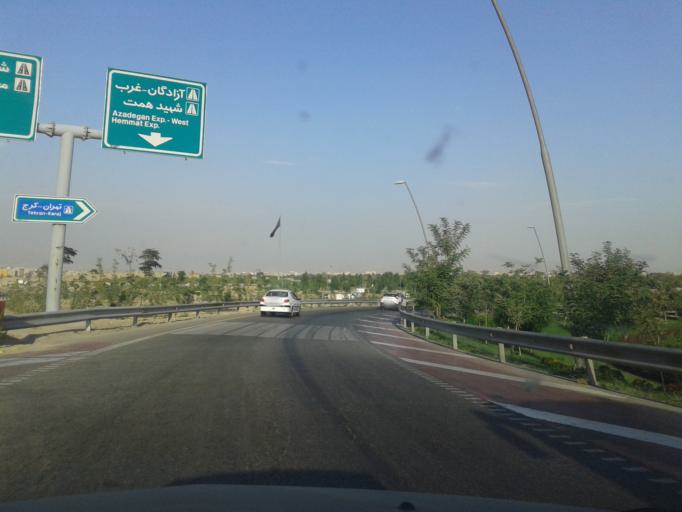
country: IR
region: Tehran
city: Eslamshahr
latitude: 35.6511
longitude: 51.2753
